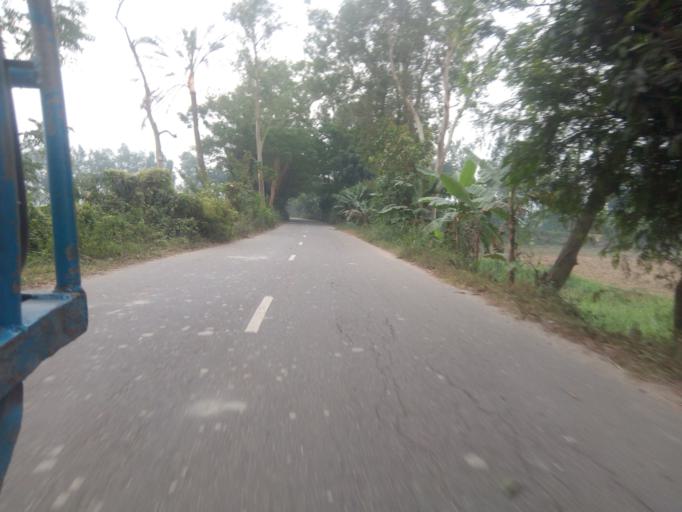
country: BD
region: Dhaka
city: Narayanganj
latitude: 23.5226
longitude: 90.4712
